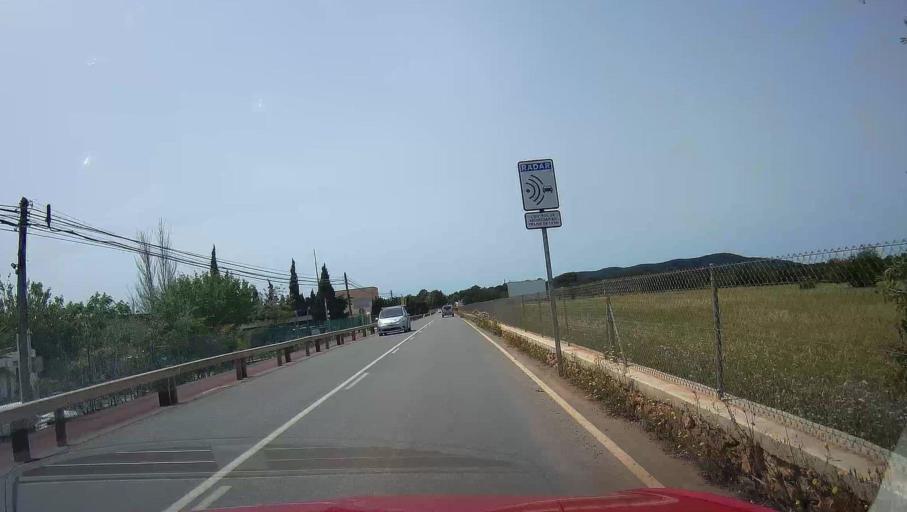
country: ES
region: Balearic Islands
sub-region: Illes Balears
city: Santa Eularia des Riu
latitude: 39.0041
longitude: 1.5699
